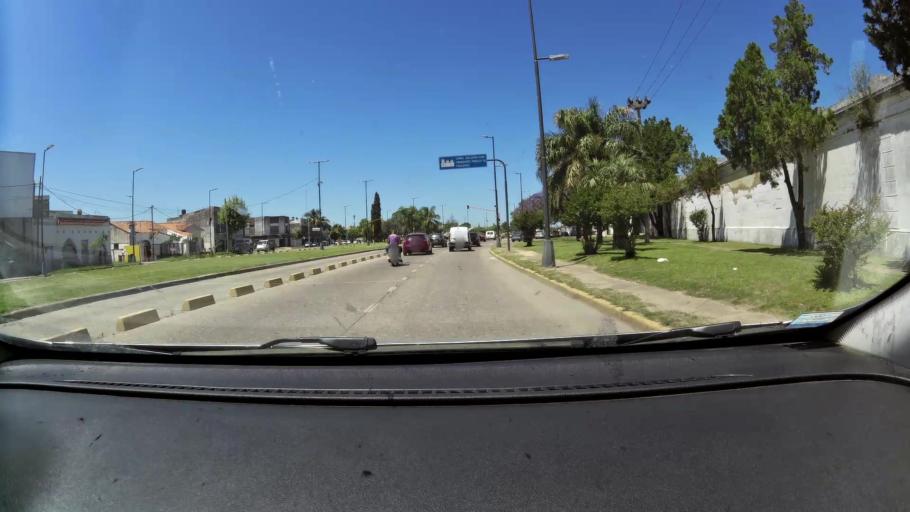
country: AR
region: Santa Fe
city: Santa Fe de la Vera Cruz
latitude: -31.6154
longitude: -60.7177
